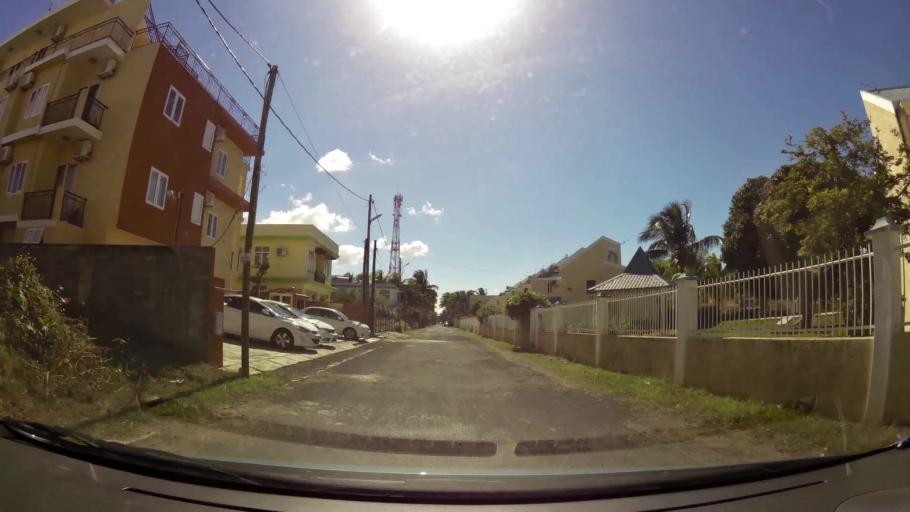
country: MU
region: Black River
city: Flic en Flac
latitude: -20.2930
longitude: 57.3650
